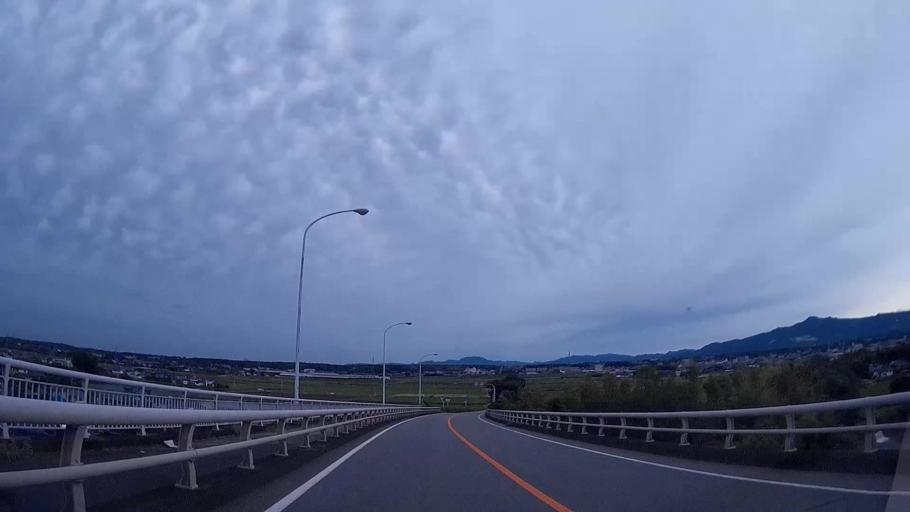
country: JP
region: Kumamoto
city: Ozu
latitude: 32.8535
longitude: 130.8554
